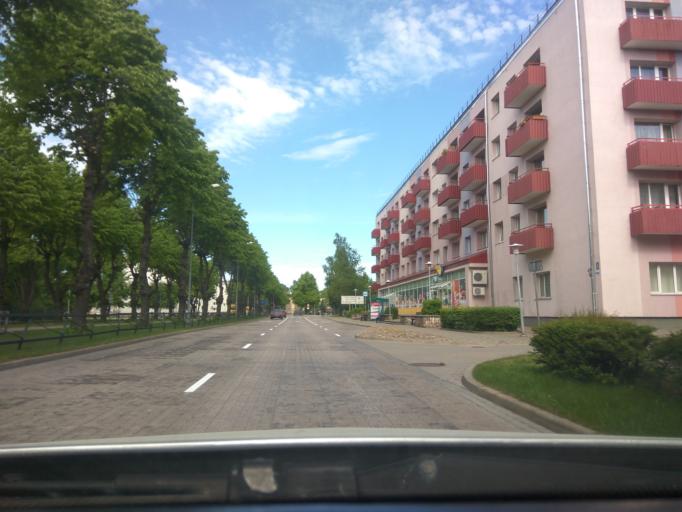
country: LV
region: Ventspils
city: Ventspils
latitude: 57.3921
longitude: 21.5753
